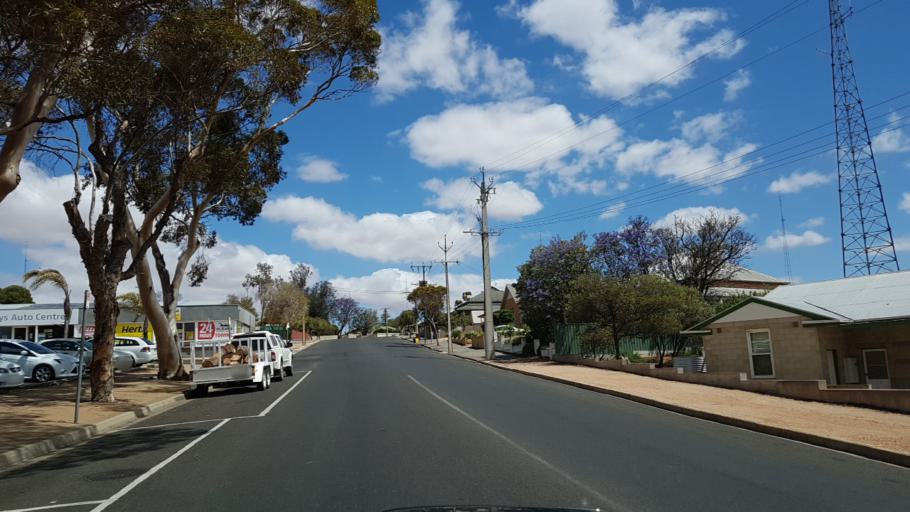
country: AU
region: South Australia
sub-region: Loxton Waikerie
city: Waikerie
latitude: -34.1796
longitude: 139.9841
